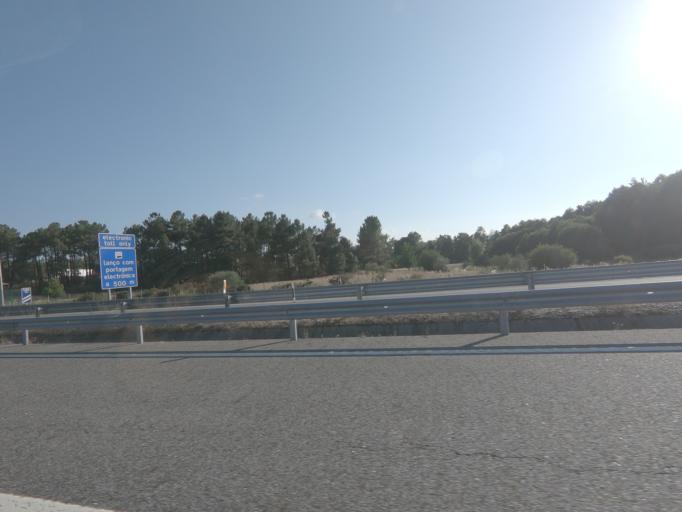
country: PT
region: Vila Real
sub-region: Chaves
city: Chaves
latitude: 41.8135
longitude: -7.4136
